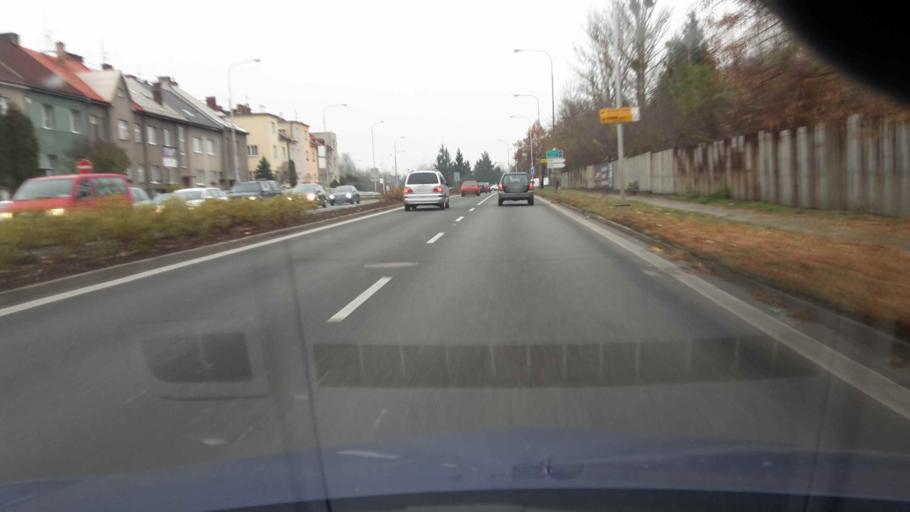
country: CZ
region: Olomoucky
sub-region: Okres Olomouc
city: Olomouc
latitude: 49.5972
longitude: 17.2319
